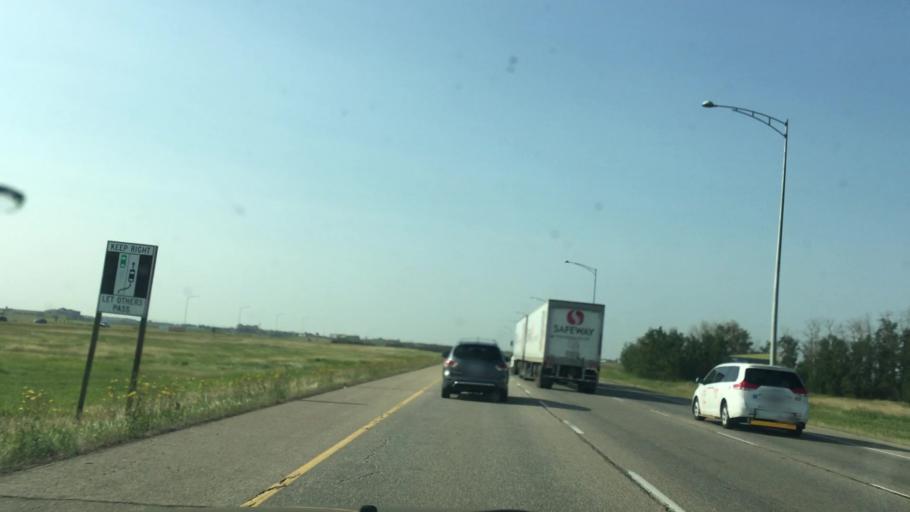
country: CA
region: Alberta
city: Leduc
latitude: 53.3250
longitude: -113.5498
